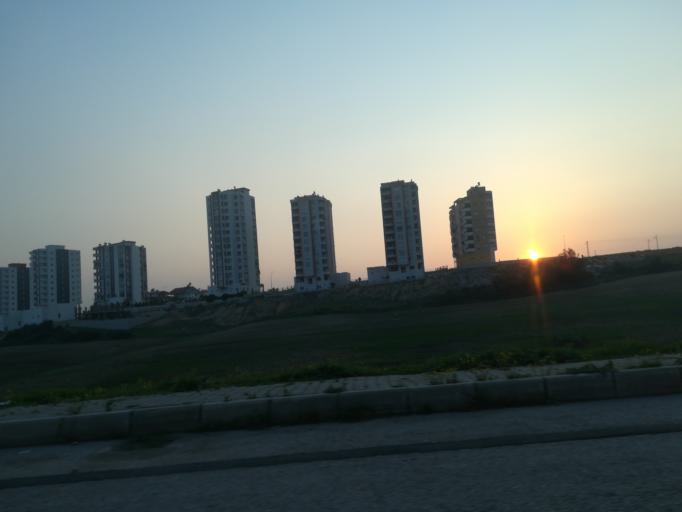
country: TR
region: Adana
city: Adana
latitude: 37.0799
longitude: 35.4122
